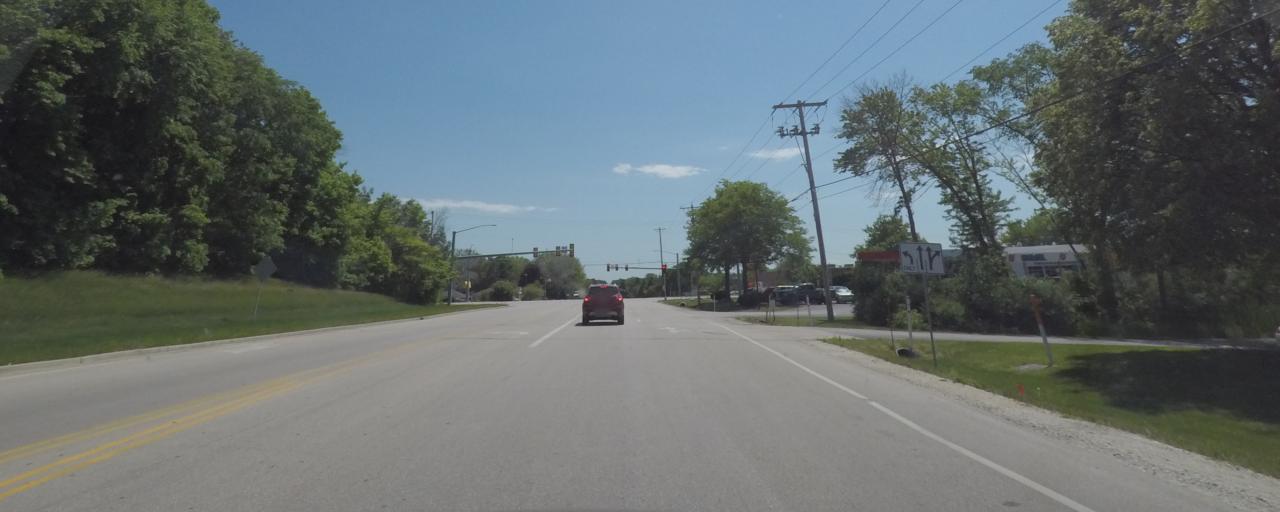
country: US
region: Wisconsin
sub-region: Waukesha County
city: New Berlin
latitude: 42.9951
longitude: -88.1280
